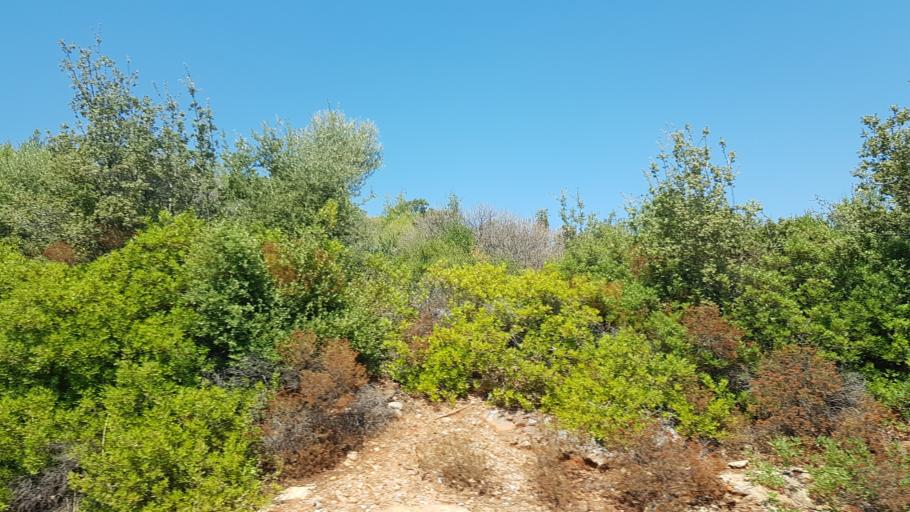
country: TR
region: Mugla
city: Karaova
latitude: 37.0346
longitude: 27.7354
